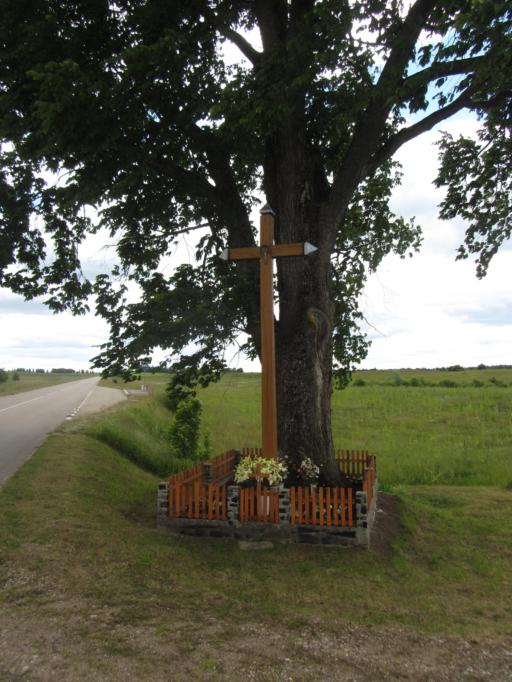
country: LT
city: Svencionys
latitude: 55.1828
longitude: 26.1407
